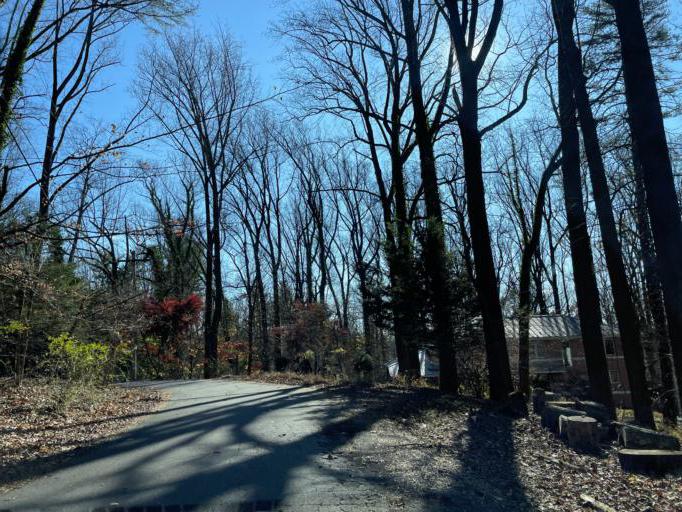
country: US
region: Maryland
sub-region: Baltimore County
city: Mays Chapel
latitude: 39.3985
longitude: -76.6609
